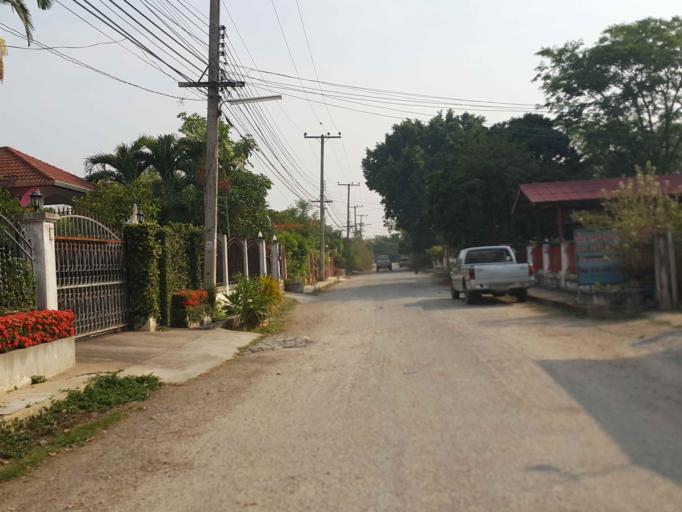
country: TH
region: Chiang Mai
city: Saraphi
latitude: 18.7673
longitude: 99.0626
